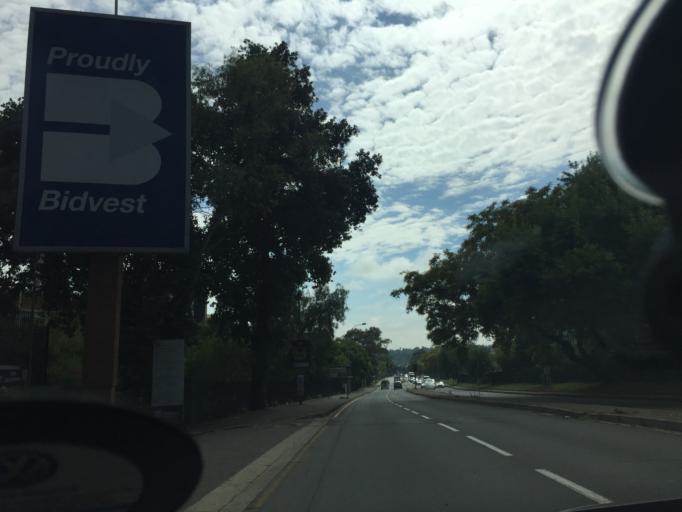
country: ZA
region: Gauteng
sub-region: City of Johannesburg Metropolitan Municipality
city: Johannesburg
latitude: -26.1324
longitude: 28.0579
